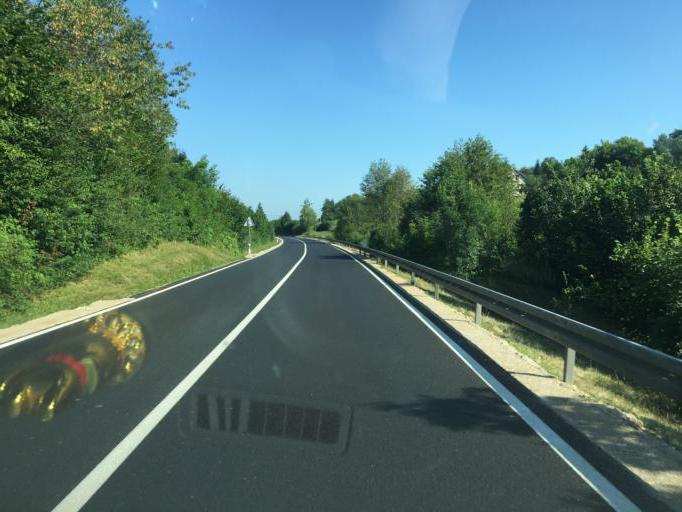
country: HR
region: Karlovacka
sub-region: Grad Karlovac
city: Slunj
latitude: 45.0184
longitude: 15.6515
